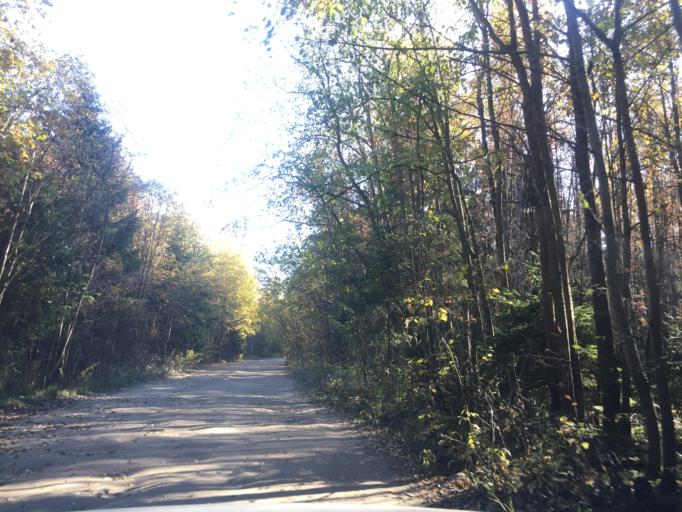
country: RU
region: Leningrad
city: Kuznechnoye
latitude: 61.3033
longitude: 30.0466
